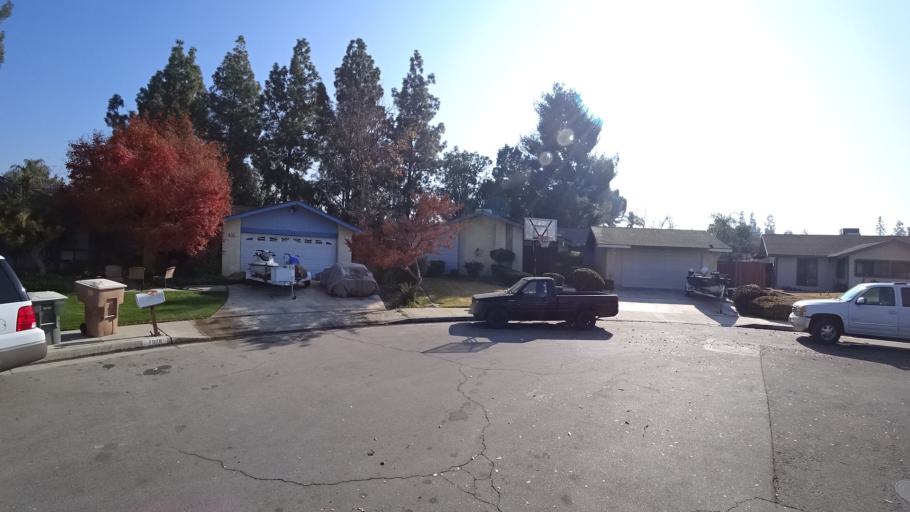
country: US
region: California
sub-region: Kern County
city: Greenacres
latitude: 35.3573
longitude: -119.0818
